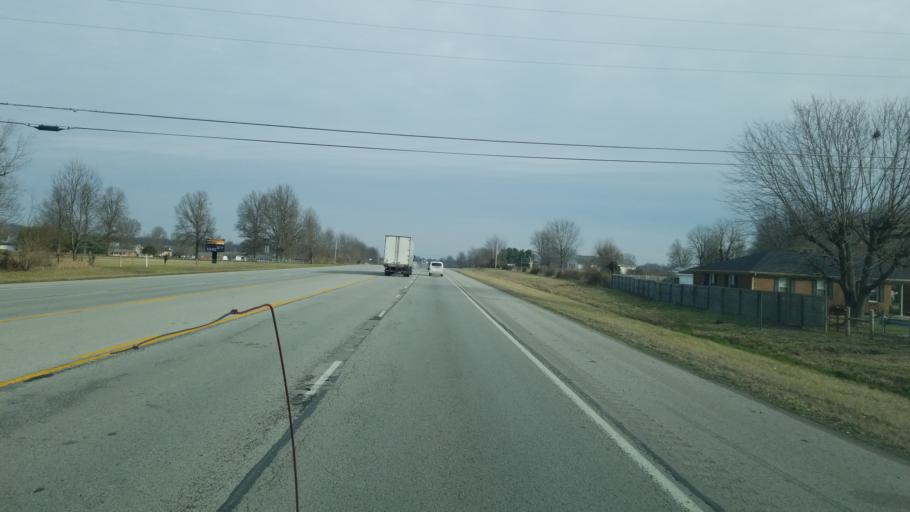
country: US
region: Kentucky
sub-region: Boyle County
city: Junction City
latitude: 37.5856
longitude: -84.7843
